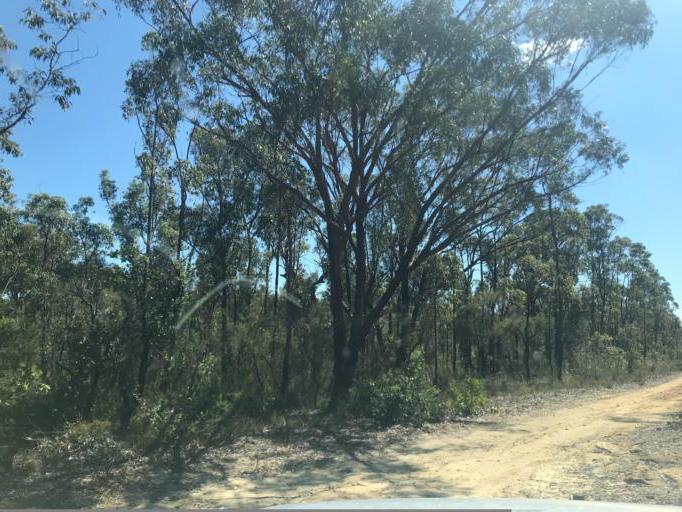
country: AU
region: New South Wales
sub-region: Wyong Shire
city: Little Jilliby
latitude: -33.1608
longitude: 151.0988
